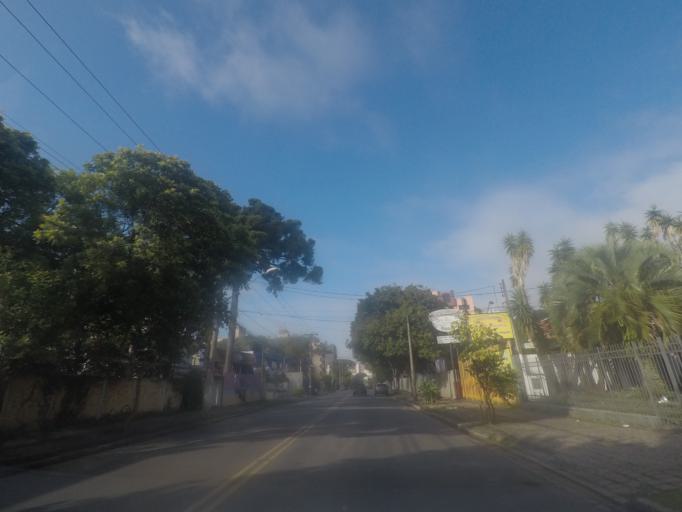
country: BR
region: Parana
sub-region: Curitiba
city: Curitiba
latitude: -25.4068
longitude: -49.2642
